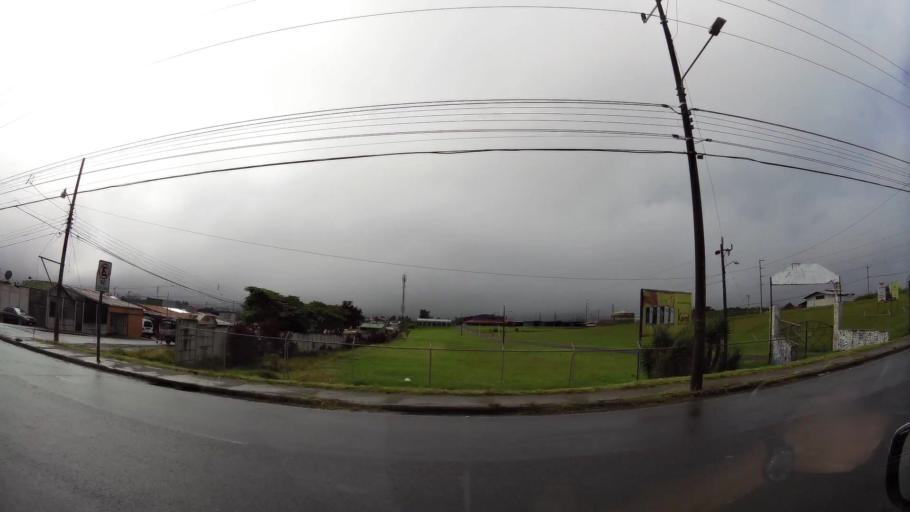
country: CR
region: Cartago
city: Paraiso
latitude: 9.8435
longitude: -83.8848
